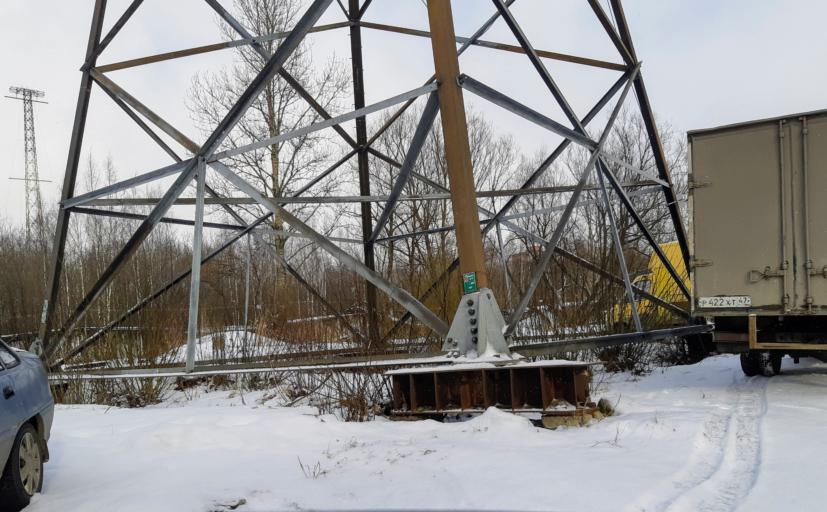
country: RU
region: St.-Petersburg
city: Obukhovo
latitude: 59.8743
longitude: 30.4668
